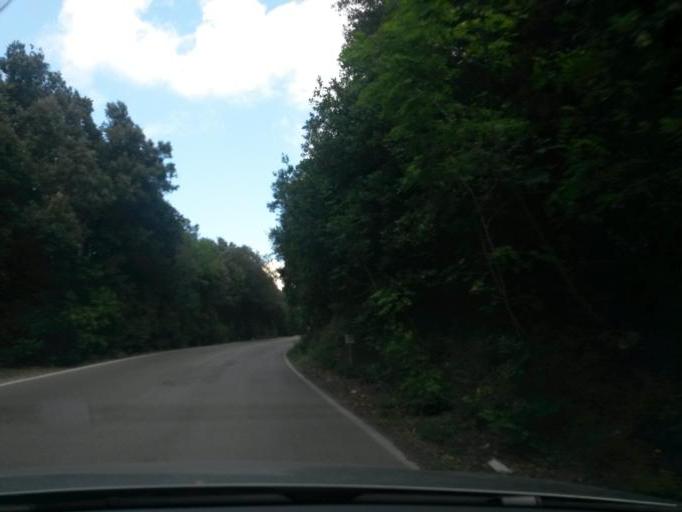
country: IT
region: Tuscany
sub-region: Provincia di Livorno
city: Marciana Marina
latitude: 42.7876
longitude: 10.2275
